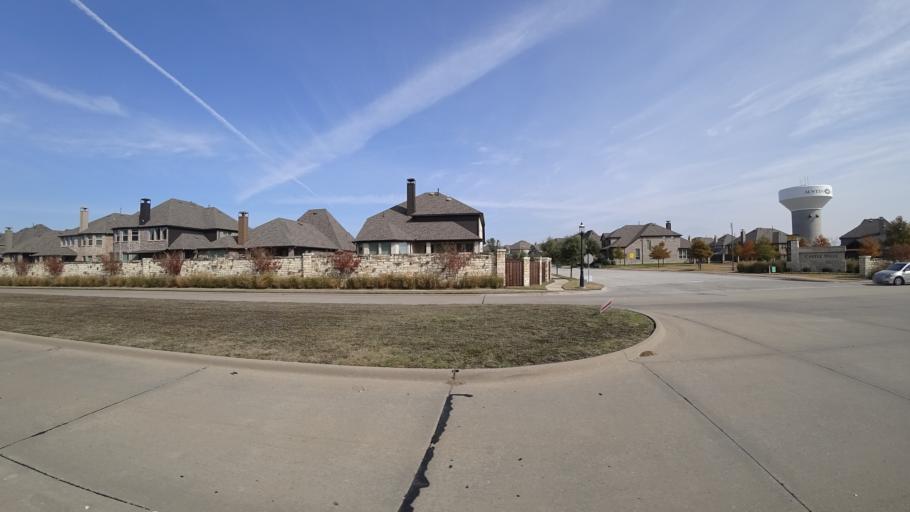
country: US
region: Texas
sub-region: Denton County
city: The Colony
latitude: 33.0623
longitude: -96.8792
